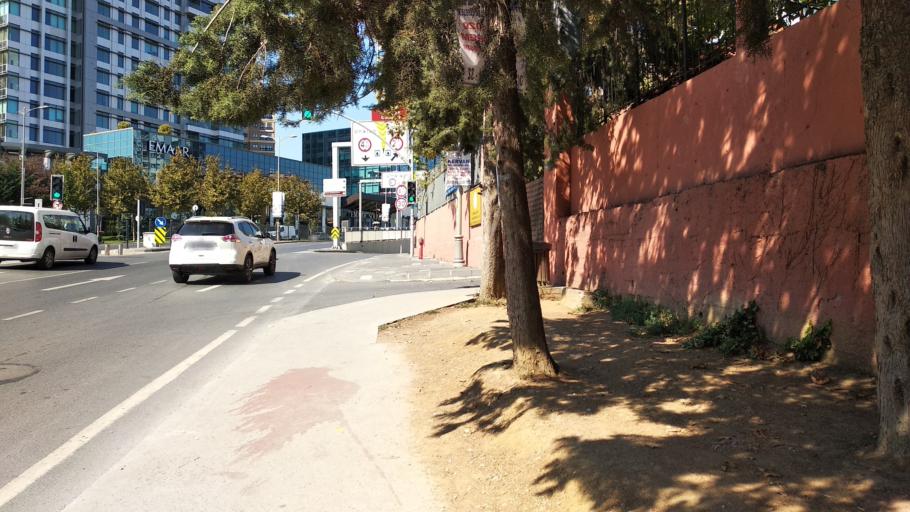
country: TR
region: Istanbul
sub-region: Atasehir
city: Atasehir
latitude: 41.0018
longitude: 29.0729
